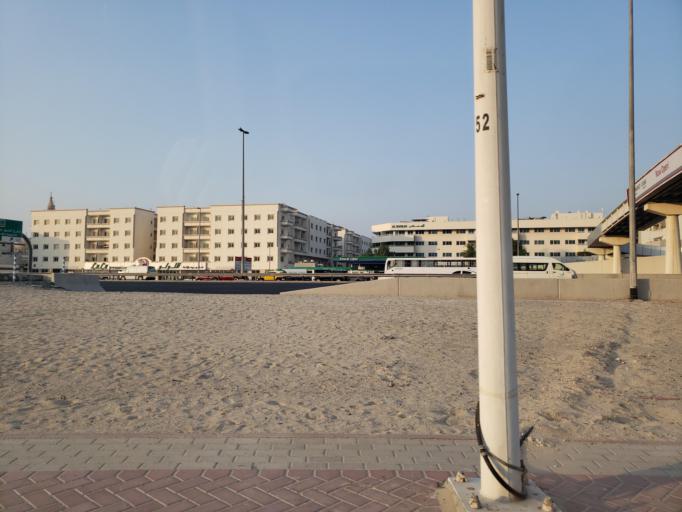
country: AE
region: Ash Shariqah
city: Sharjah
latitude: 25.2369
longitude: 55.2997
